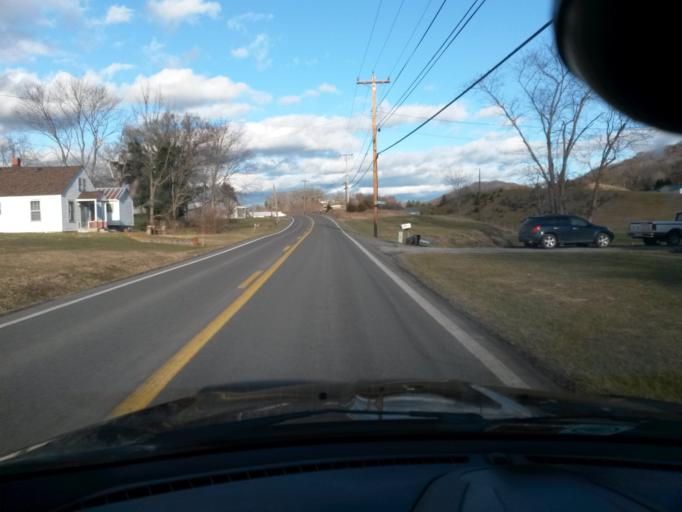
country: US
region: Virginia
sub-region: Giles County
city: Pearisburg
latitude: 37.4044
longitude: -80.7601
